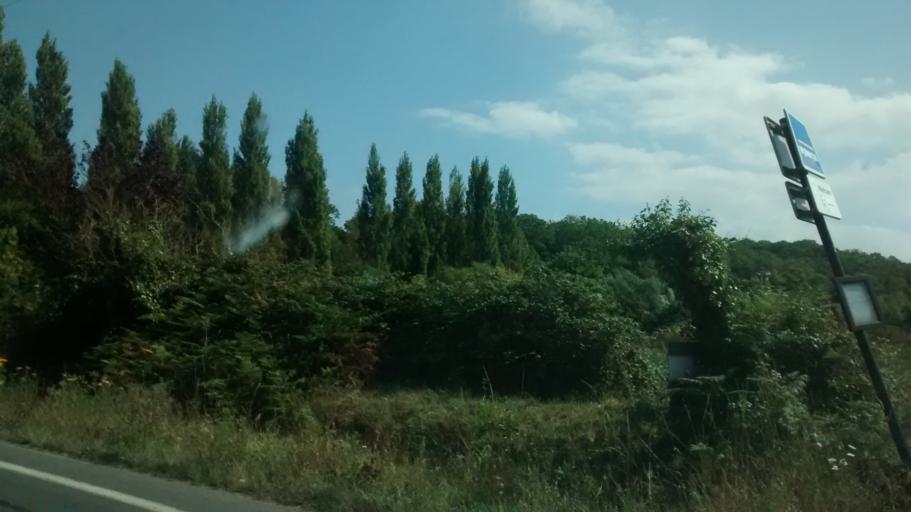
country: FR
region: Brittany
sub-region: Departement d'Ille-et-Vilaine
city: Saint-Coulomb
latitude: 48.6790
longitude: -1.8860
